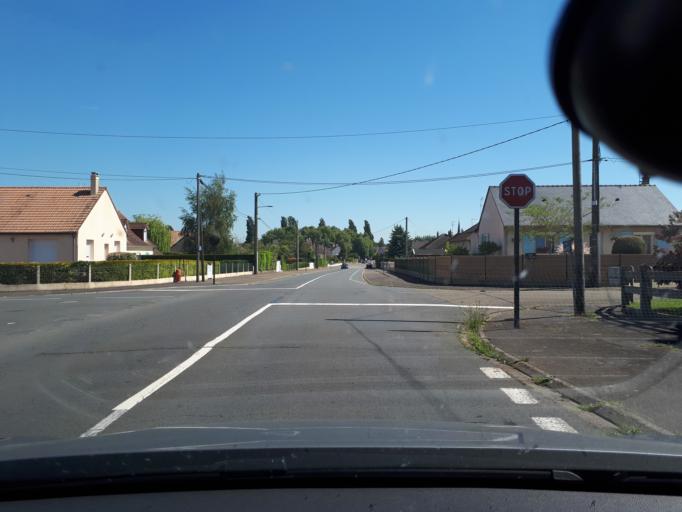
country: FR
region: Pays de la Loire
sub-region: Departement de la Sarthe
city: Champagne
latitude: 48.0743
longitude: 0.2917
